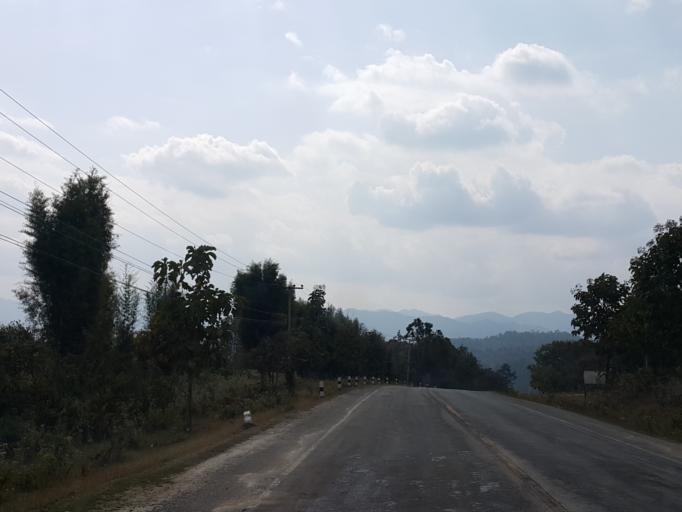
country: TH
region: Chiang Mai
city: Om Koi
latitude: 17.8326
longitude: 98.3683
